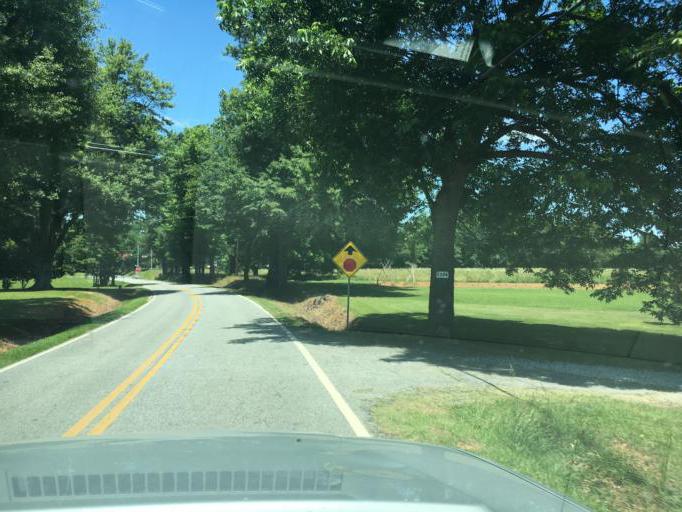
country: US
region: South Carolina
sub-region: Spartanburg County
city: Inman
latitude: 34.9939
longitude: -82.0616
